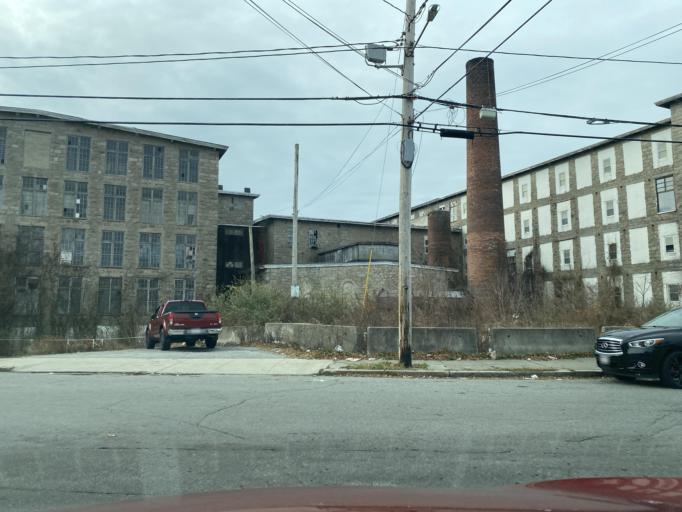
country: US
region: Massachusetts
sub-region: Bristol County
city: Fall River
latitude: 41.6894
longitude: -71.1353
